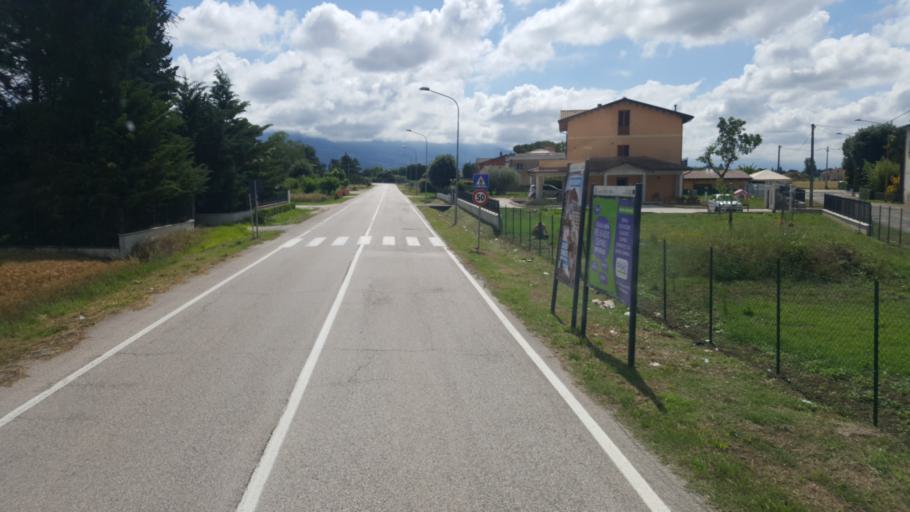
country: IT
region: Umbria
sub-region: Provincia di Perugia
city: Ospedalicchio
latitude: 43.0642
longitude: 12.5175
